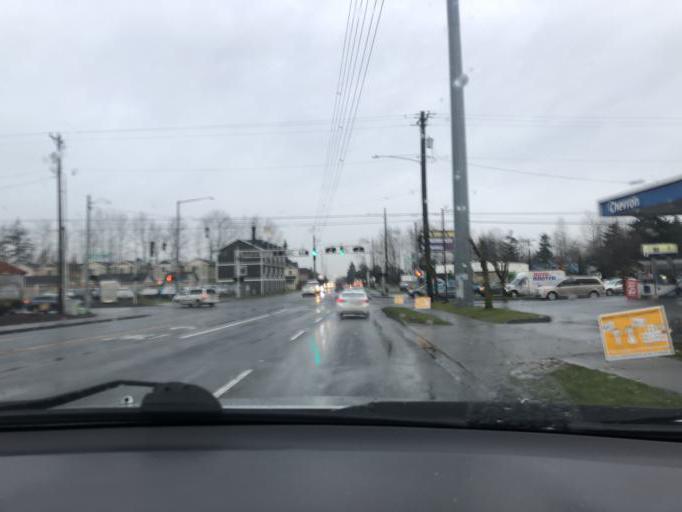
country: US
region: Washington
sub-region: Pierce County
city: Midland
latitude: 47.1918
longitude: -122.4203
